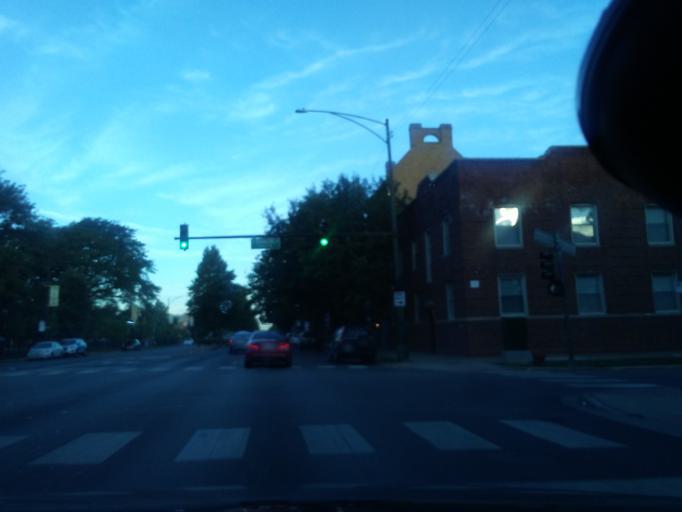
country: US
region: Illinois
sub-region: Cook County
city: Lincolnwood
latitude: 41.9538
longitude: -87.7226
